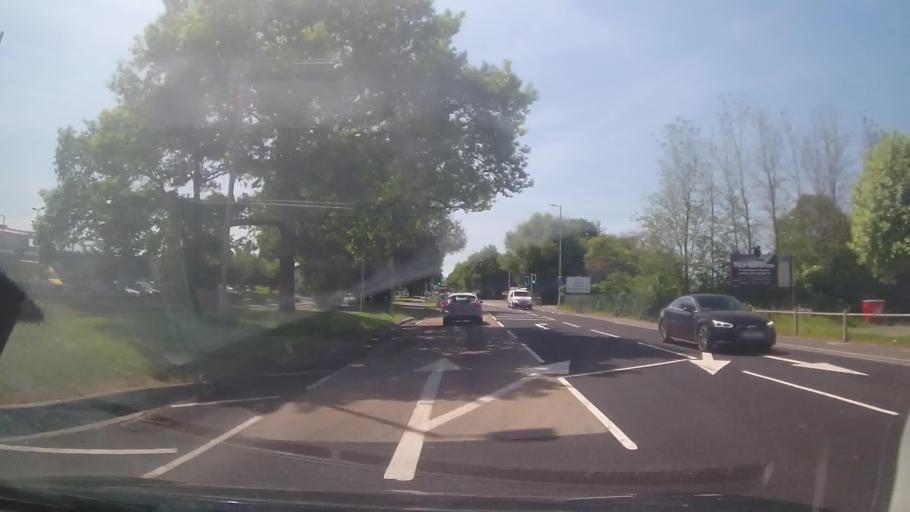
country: GB
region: England
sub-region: Herefordshire
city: Hereford
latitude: 52.0715
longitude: -2.7222
